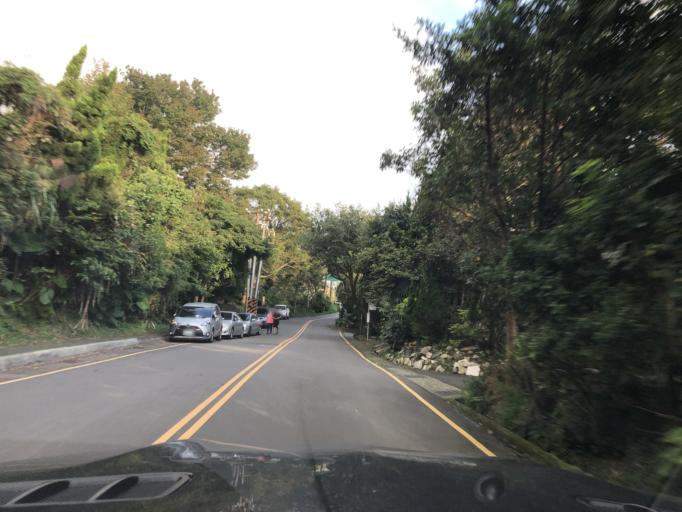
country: TW
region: Taipei
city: Taipei
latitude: 25.1516
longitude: 121.5610
